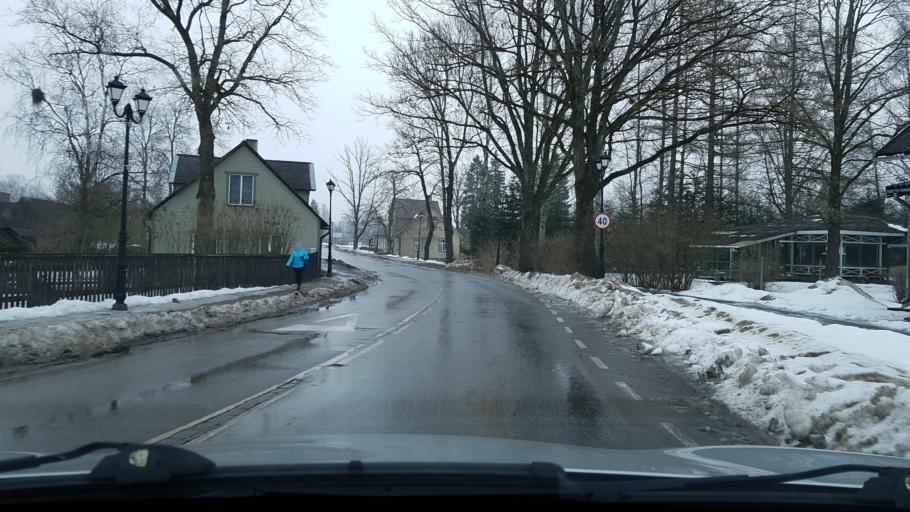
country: EE
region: Valgamaa
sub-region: Torva linn
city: Torva
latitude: 58.2349
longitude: 25.8630
